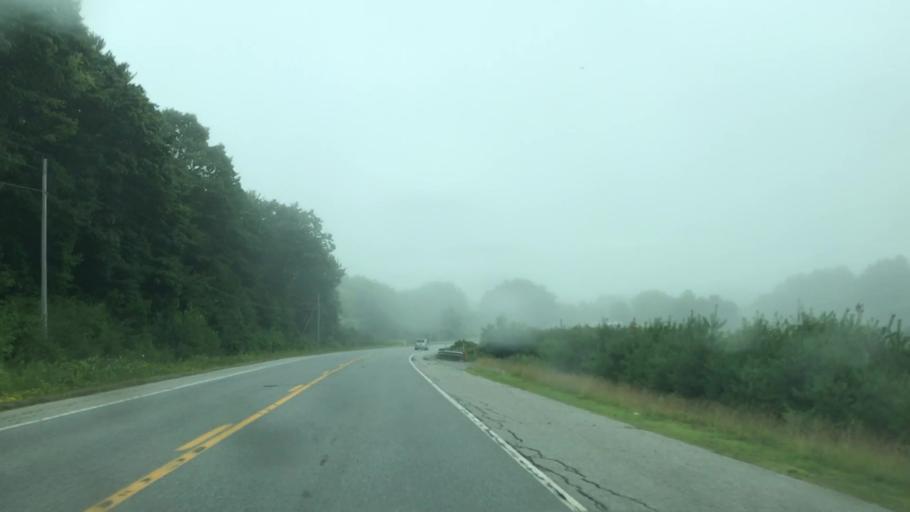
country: US
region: Maine
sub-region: Knox County
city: Rockport
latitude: 44.1747
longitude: -69.1511
